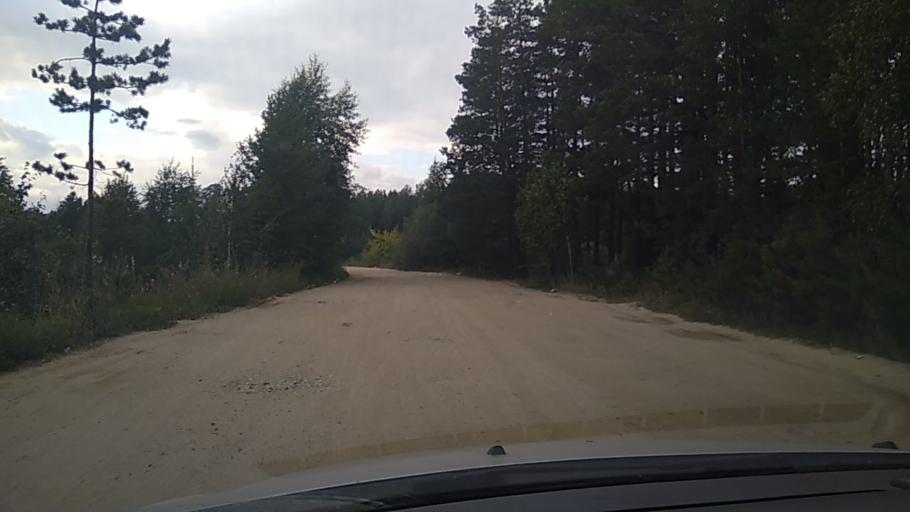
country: RU
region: Chelyabinsk
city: Kyshtym
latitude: 55.6829
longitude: 60.5723
